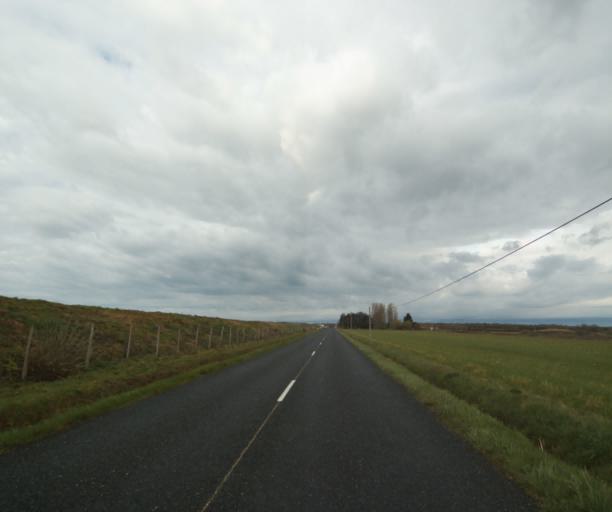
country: FR
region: Auvergne
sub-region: Departement de l'Allier
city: Neuilly-le-Real
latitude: 46.5371
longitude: 3.4360
